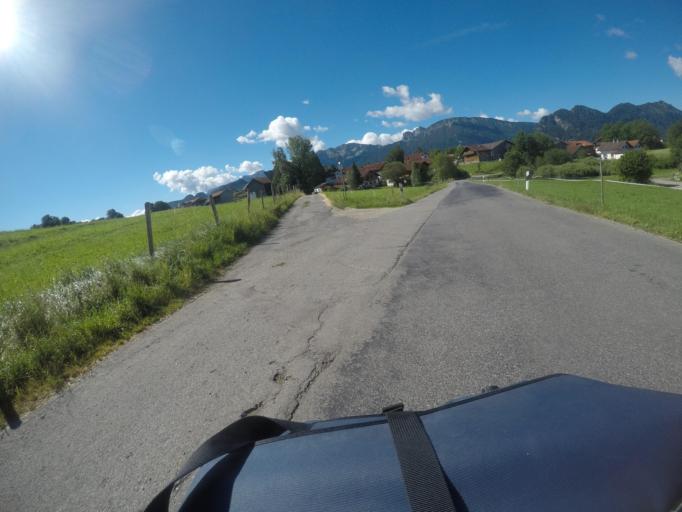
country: DE
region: Bavaria
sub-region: Swabia
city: Pfronten
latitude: 47.5991
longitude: 10.5668
